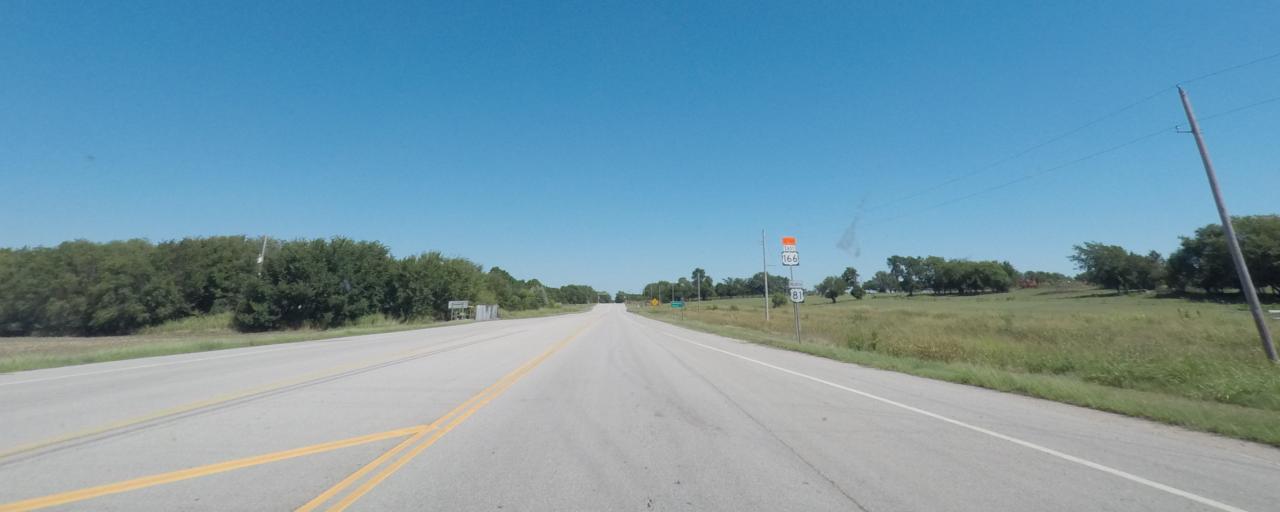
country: US
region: Kansas
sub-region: Sumner County
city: Caldwell
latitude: 37.0574
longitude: -97.4012
